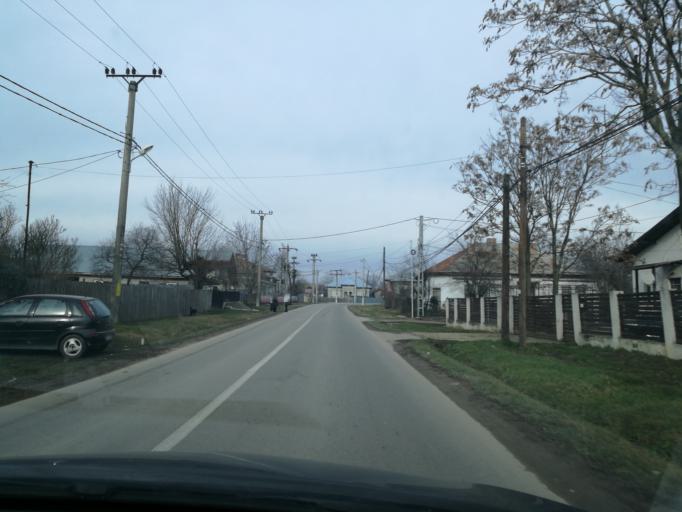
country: RO
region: Ialomita
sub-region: Comuna Fierbinti-Targ
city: Fierbintii de Jos
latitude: 44.6907
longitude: 26.3945
